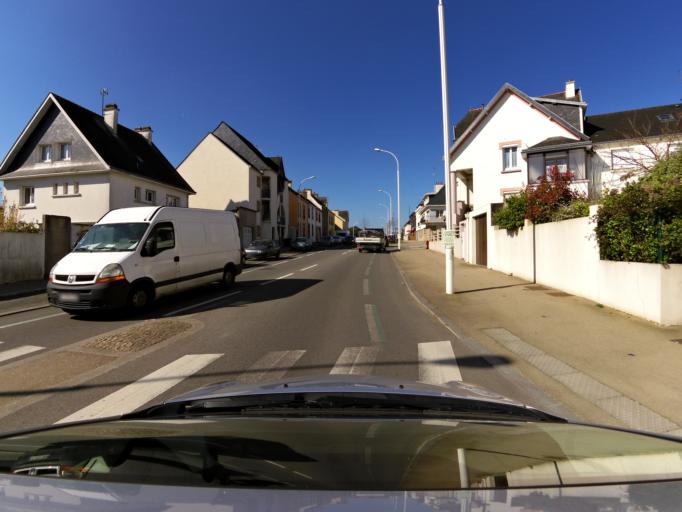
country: FR
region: Brittany
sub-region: Departement du Morbihan
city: Lorient
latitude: 47.7467
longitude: -3.3779
